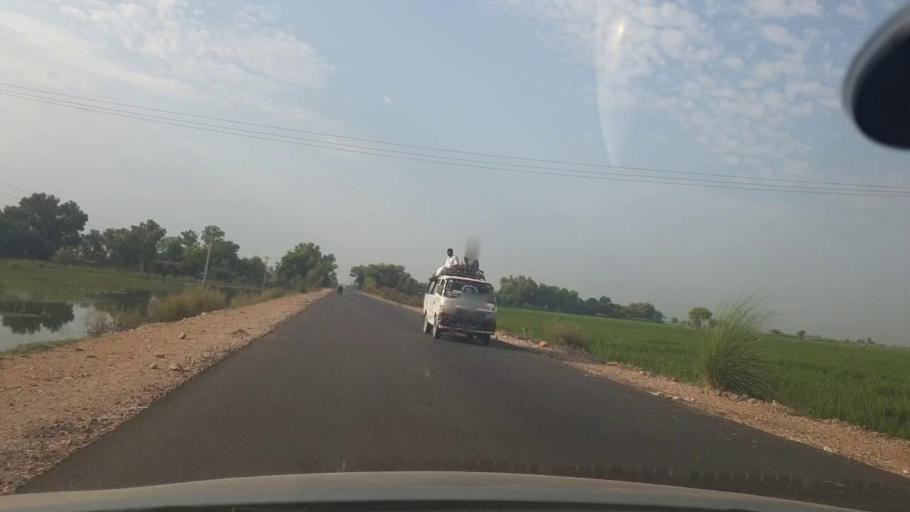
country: PK
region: Sindh
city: Jacobabad
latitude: 28.1132
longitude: 68.3268
